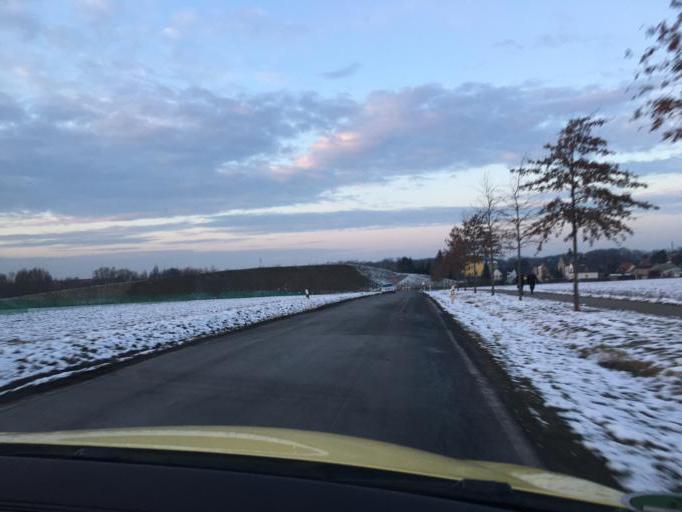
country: DE
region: Saxony
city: Taucha
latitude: 51.3198
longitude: 12.4519
